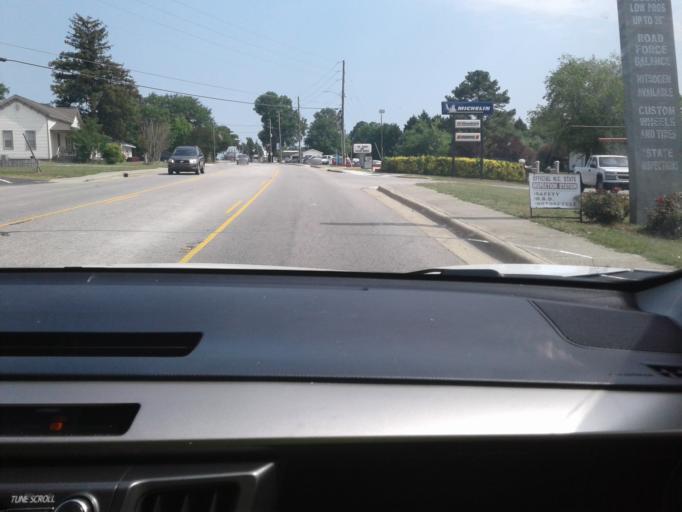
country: US
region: North Carolina
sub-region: Harnett County
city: Coats
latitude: 35.4023
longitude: -78.6722
